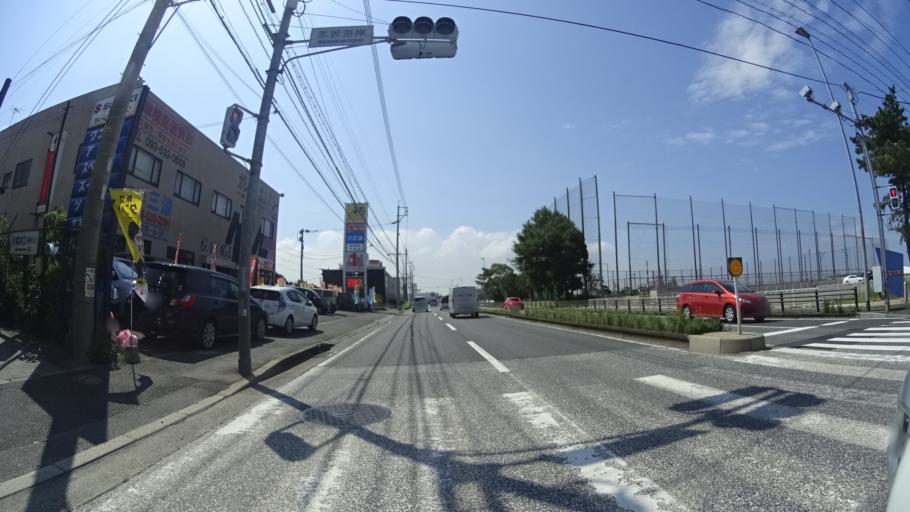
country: JP
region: Yamaguchi
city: Shimonoseki
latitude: 33.8925
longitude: 130.9069
